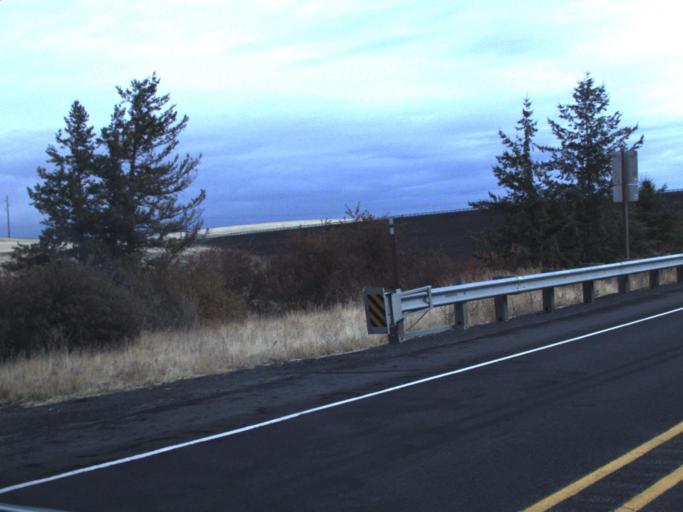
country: US
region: Washington
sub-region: Asotin County
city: Clarkston
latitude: 46.4742
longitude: -117.0432
